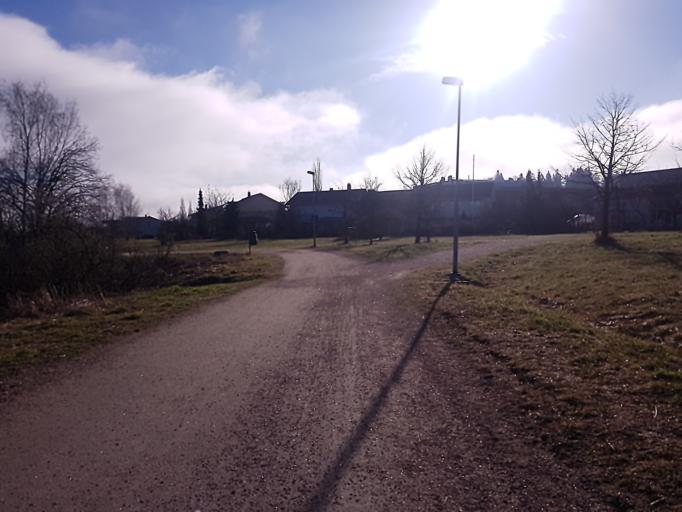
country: FI
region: Uusimaa
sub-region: Helsinki
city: Helsinki
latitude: 60.2641
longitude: 24.9479
